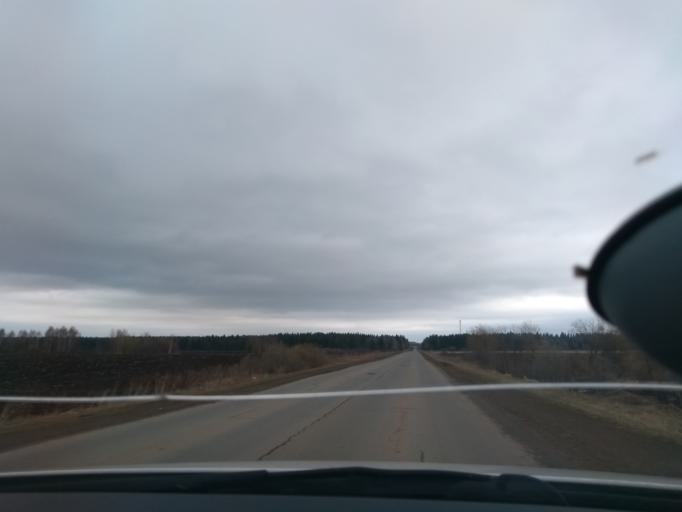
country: RU
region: Perm
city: Kungur
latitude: 57.3904
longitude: 56.8665
